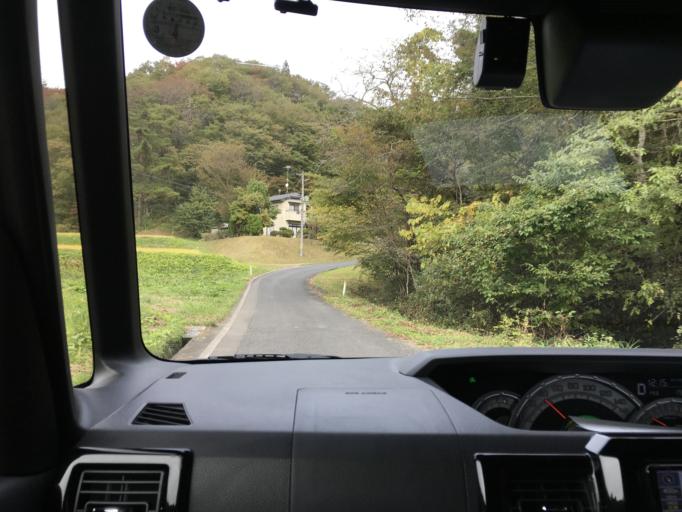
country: JP
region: Iwate
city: Mizusawa
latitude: 39.0252
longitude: 141.3539
